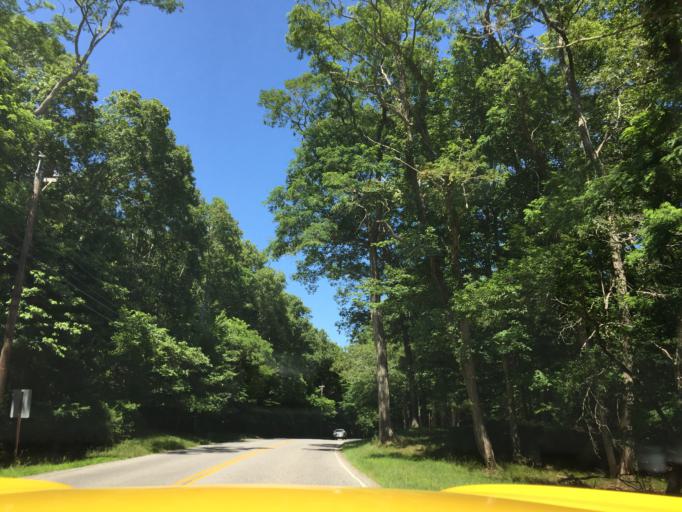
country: US
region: New York
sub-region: Suffolk County
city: Amagansett
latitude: 40.9936
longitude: -72.1349
